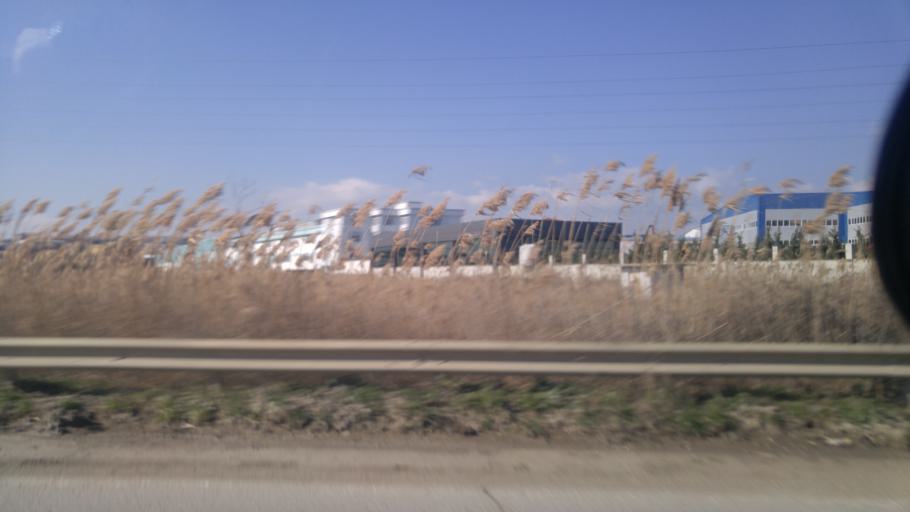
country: TR
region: Istanbul
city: Canta
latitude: 41.0718
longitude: 28.1042
